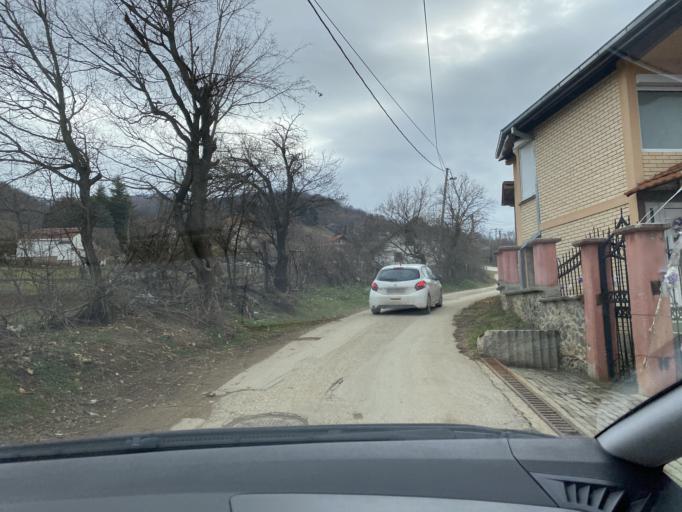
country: MK
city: Radishani
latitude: 42.1056
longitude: 21.4587
